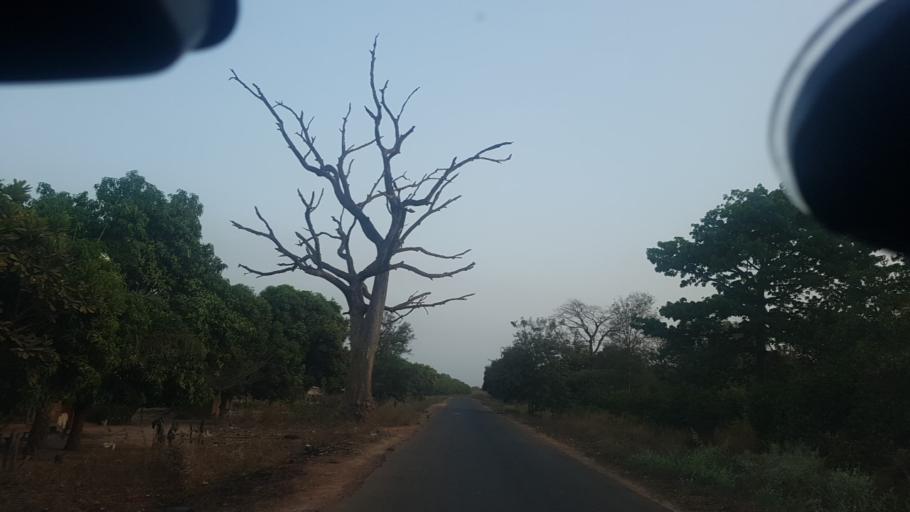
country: SN
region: Ziguinchor
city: Adeane
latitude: 12.3815
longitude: -15.7797
